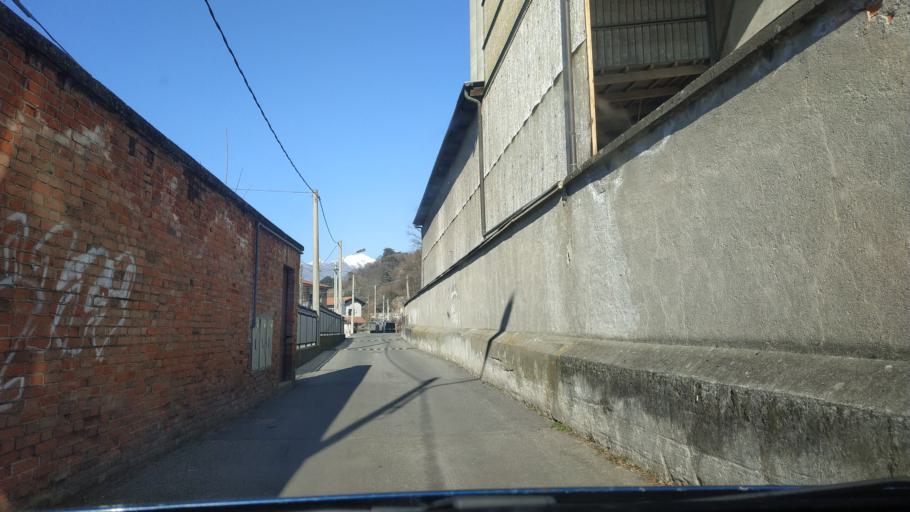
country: IT
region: Piedmont
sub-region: Provincia di Torino
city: Montalto Dora
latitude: 45.4909
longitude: 7.8671
